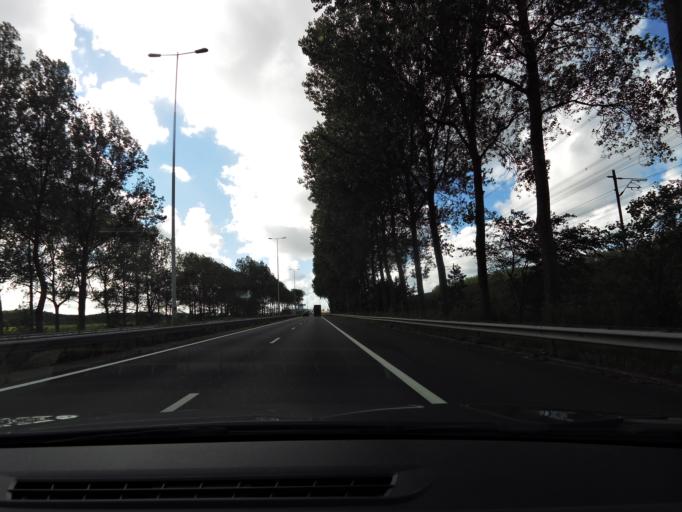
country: NL
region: South Holland
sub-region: Gemeente Rotterdam
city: Hoek van Holland
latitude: 51.9365
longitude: 4.1258
